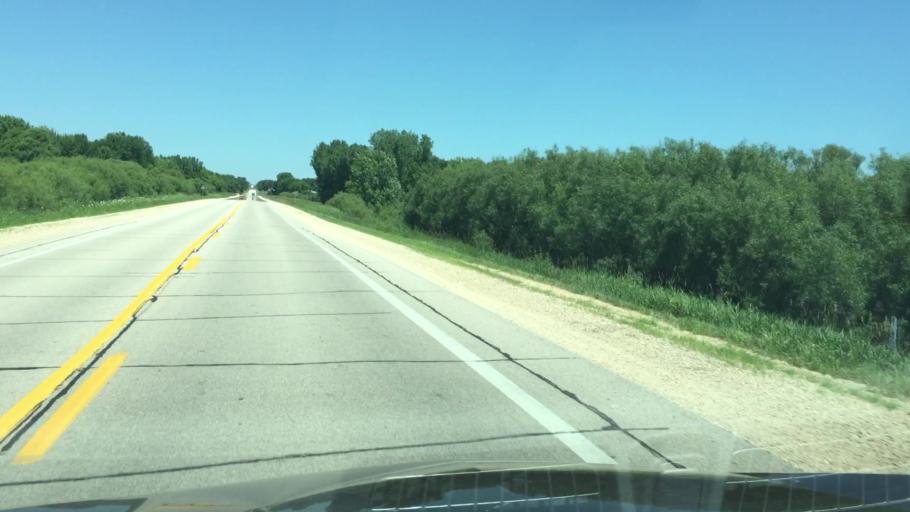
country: US
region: Iowa
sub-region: Cedar County
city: Mechanicsville
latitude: 42.0124
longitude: -91.1367
